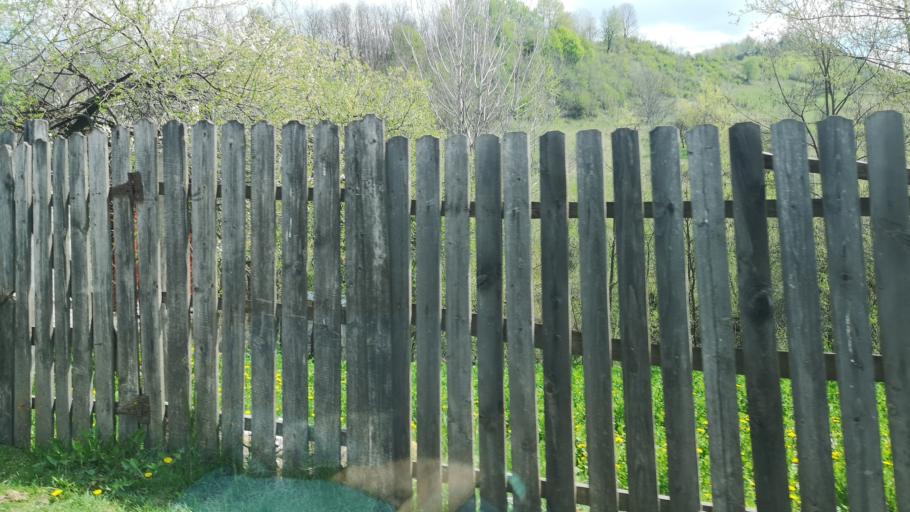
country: RO
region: Prahova
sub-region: Comuna Soimari
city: Soimari
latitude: 45.1812
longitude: 26.2173
